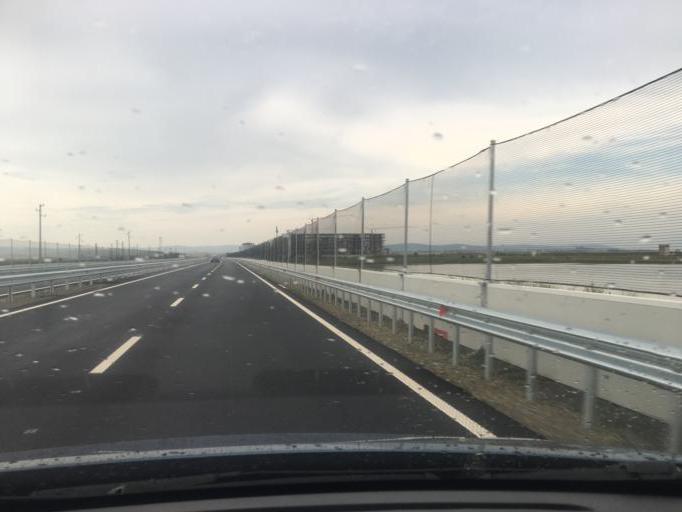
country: BG
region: Burgas
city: Aheloy
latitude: 42.6226
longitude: 27.6285
